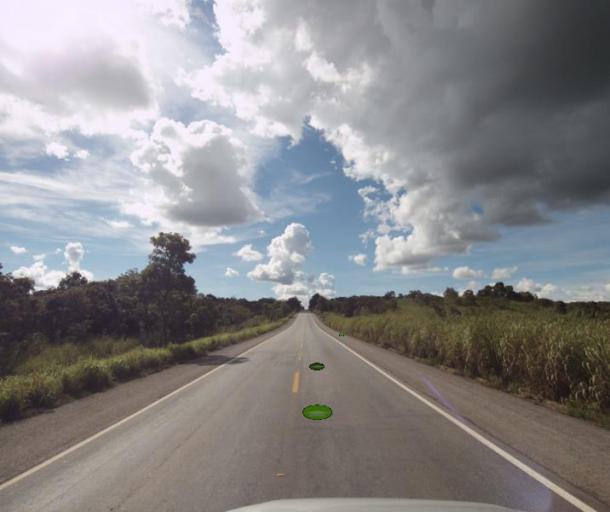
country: BR
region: Goias
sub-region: Porangatu
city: Porangatu
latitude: -13.1466
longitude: -49.1858
